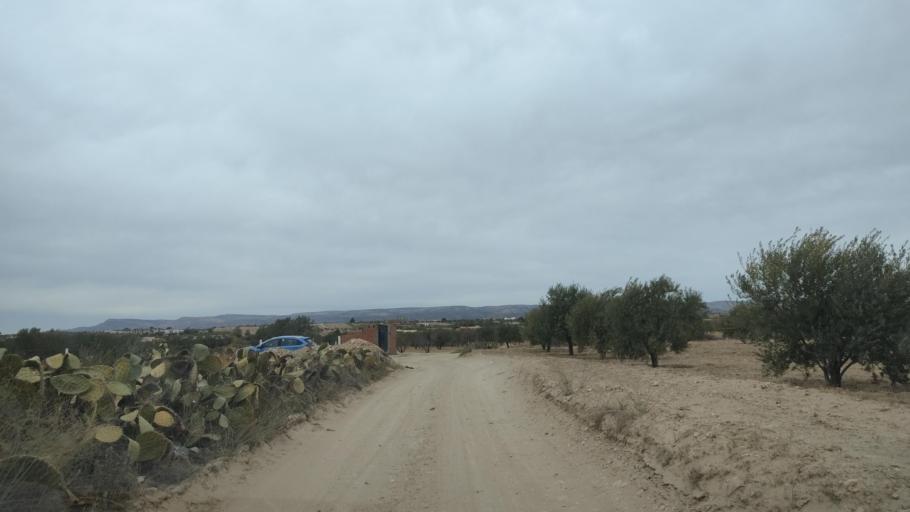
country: TN
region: Al Qasrayn
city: Kasserine
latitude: 35.2264
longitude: 8.9216
